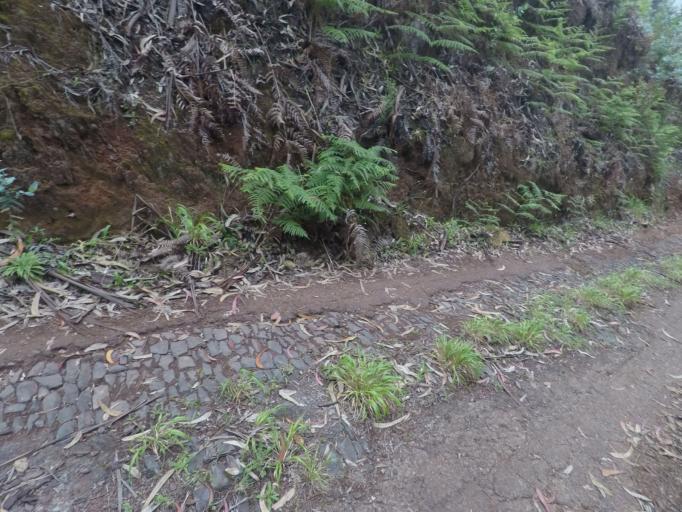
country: PT
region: Madeira
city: Ponta do Sol
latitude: 32.7212
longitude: -17.0926
